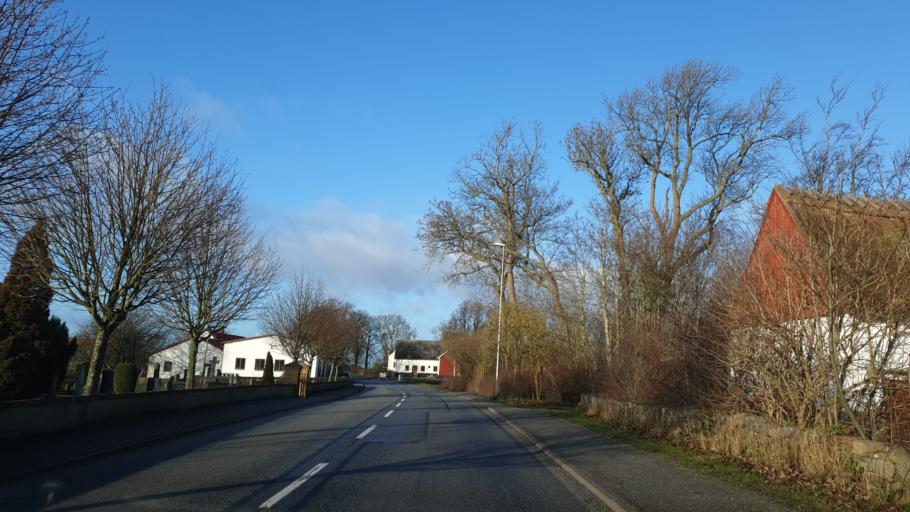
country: SE
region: Skane
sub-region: Vellinge Kommun
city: Vellinge
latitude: 55.5024
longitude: 13.0303
